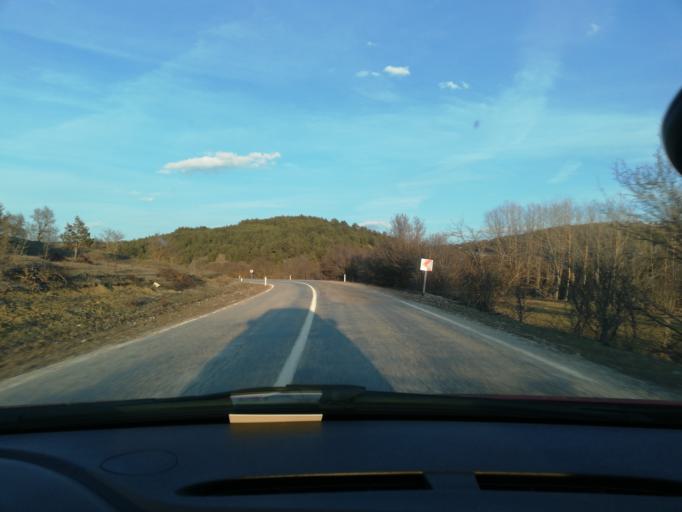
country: TR
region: Kastamonu
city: Agli
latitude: 41.6959
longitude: 33.6286
